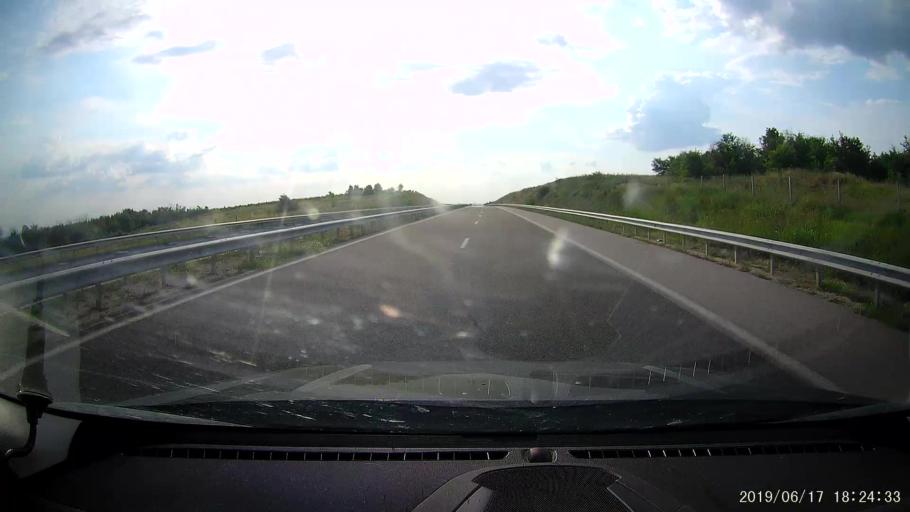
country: BG
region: Khaskovo
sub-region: Obshtina Dimitrovgrad
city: Dimitrovgrad
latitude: 41.9857
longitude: 25.6883
